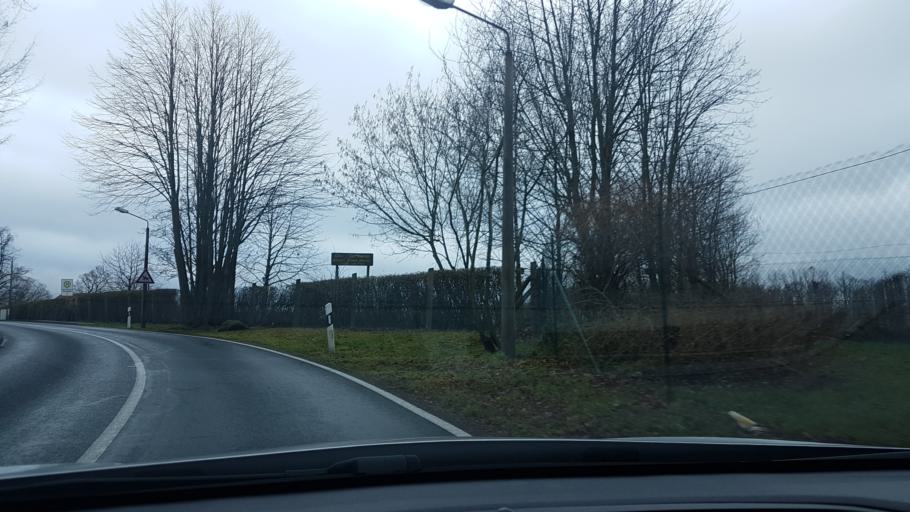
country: DE
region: Saxony
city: Goerlitz
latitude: 51.1318
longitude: 14.9585
